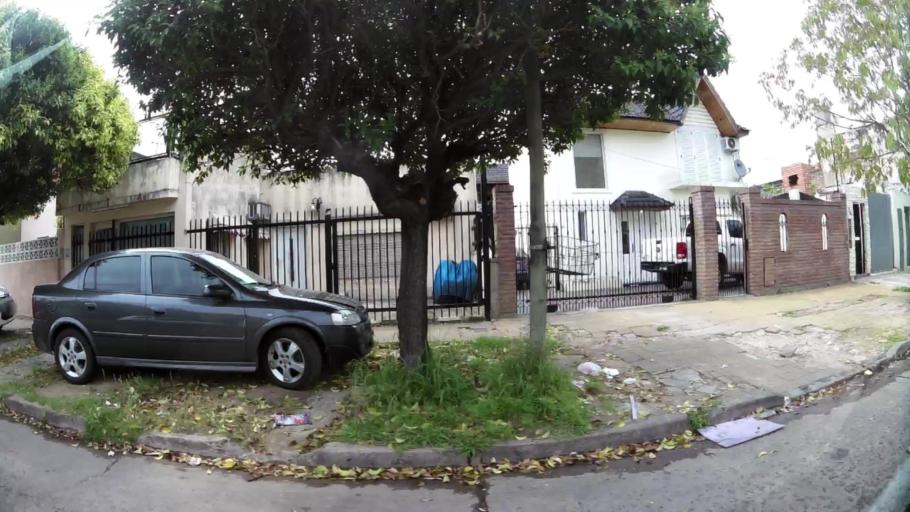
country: AR
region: Buenos Aires F.D.
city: Villa Lugano
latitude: -34.6951
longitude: -58.5126
